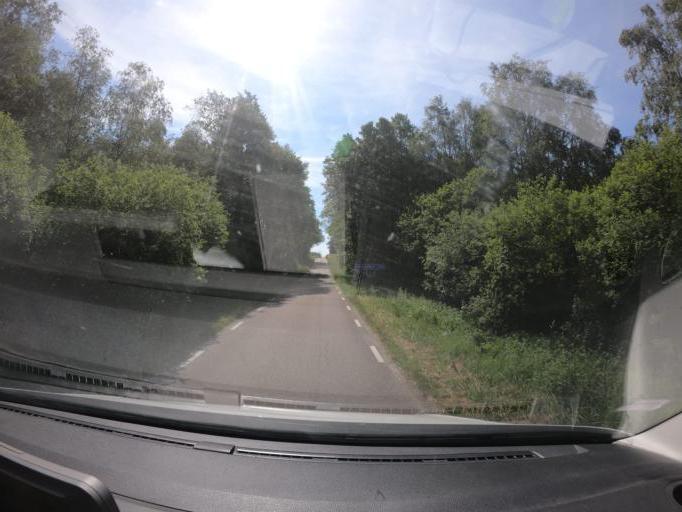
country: SE
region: Skane
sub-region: Bastads Kommun
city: Bastad
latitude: 56.3865
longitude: 12.9645
